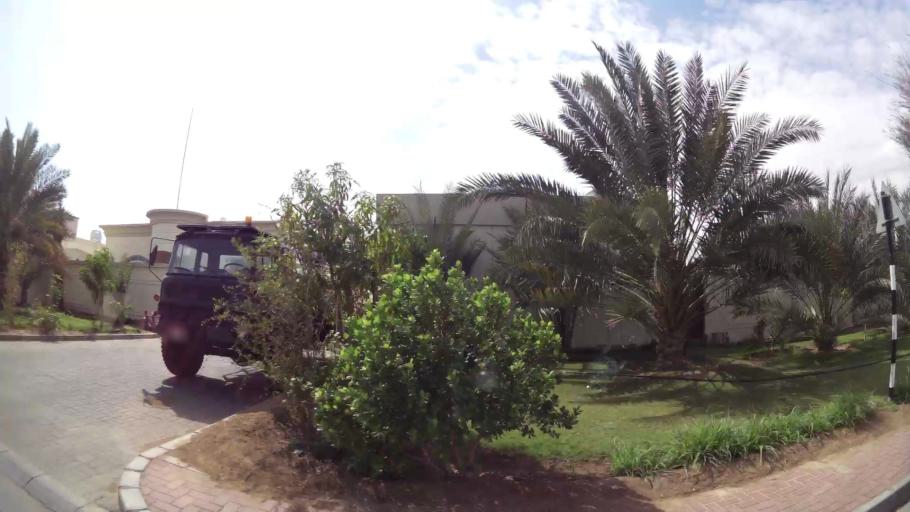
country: AE
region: Abu Dhabi
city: Al Ain
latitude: 24.1947
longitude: 55.7989
